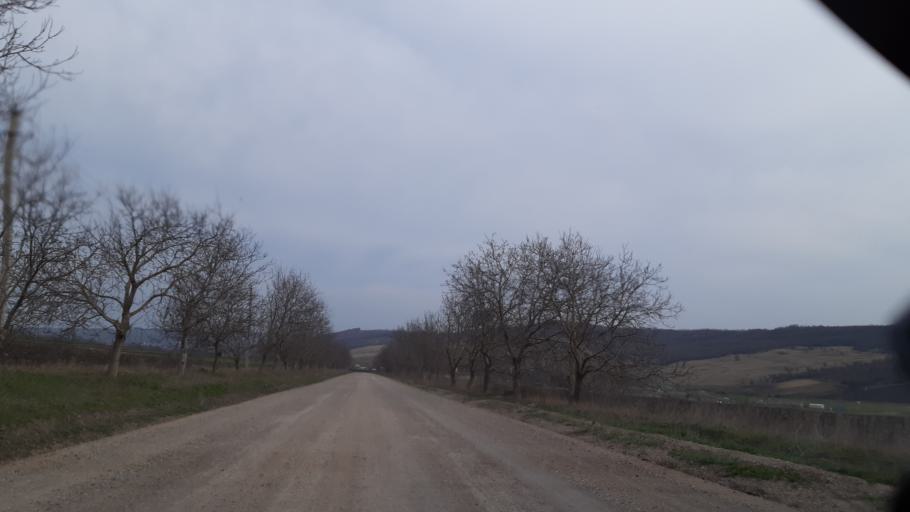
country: MD
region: Soldanesti
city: Soldanesti
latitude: 47.6910
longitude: 28.7400
